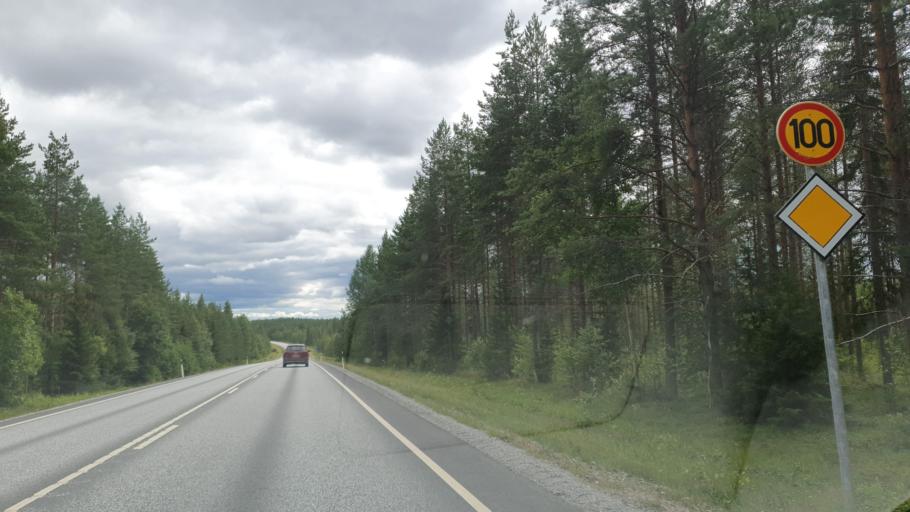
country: FI
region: Northern Savo
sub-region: Ylae-Savo
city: Sonkajaervi
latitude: 63.9184
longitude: 27.3831
